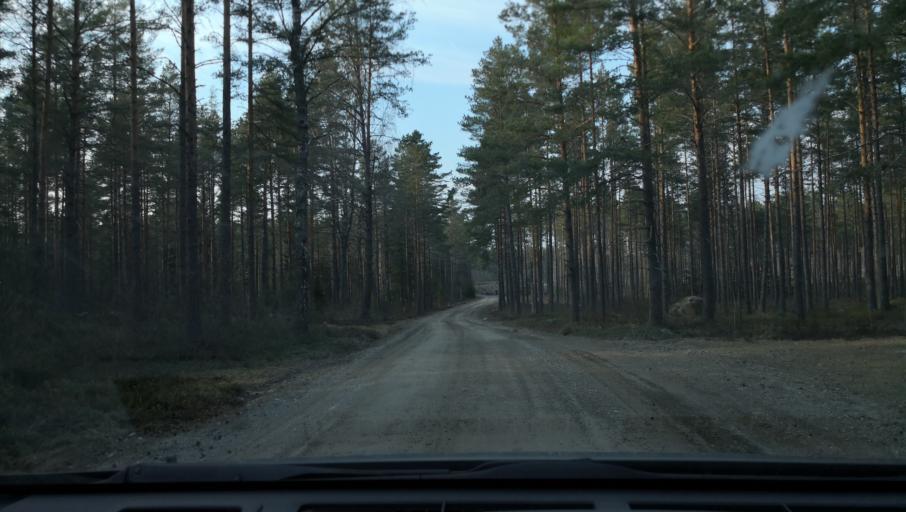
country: SE
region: OErebro
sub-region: Lindesbergs Kommun
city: Frovi
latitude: 59.3651
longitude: 15.3270
